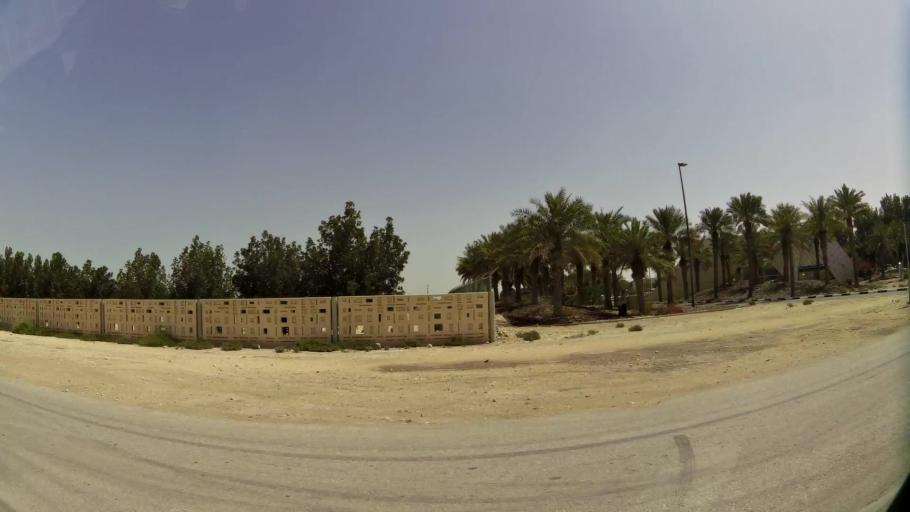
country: QA
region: Baladiyat ar Rayyan
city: Ar Rayyan
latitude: 25.3629
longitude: 51.4790
